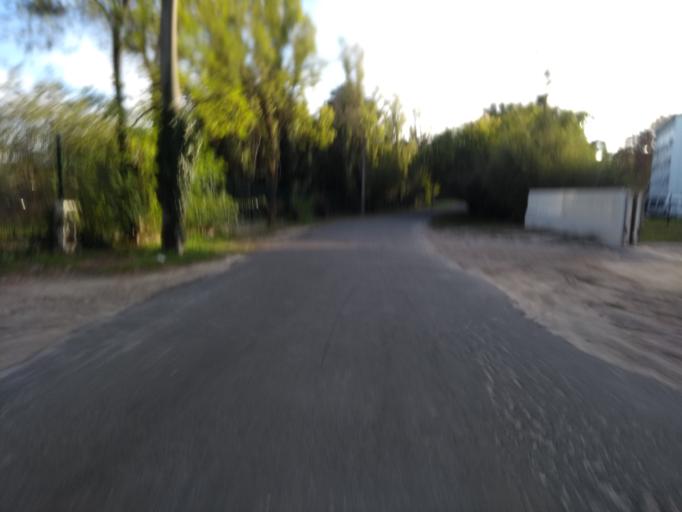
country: FR
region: Aquitaine
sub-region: Departement de la Gironde
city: Gradignan
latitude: 44.7833
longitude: -0.5983
